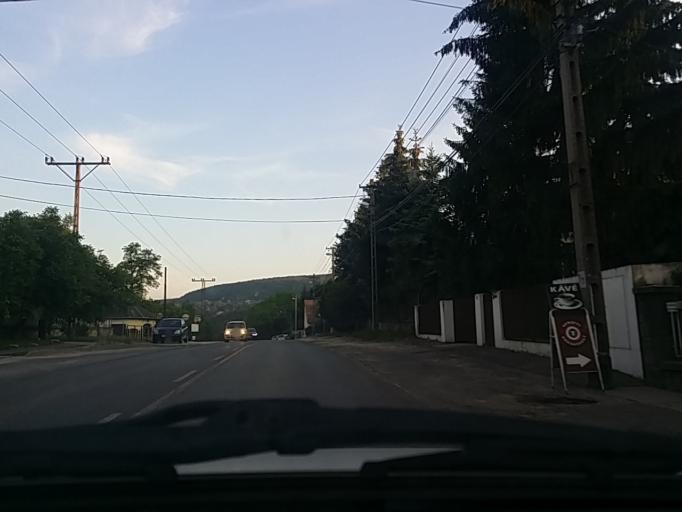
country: HU
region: Pest
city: Solymar
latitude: 47.5822
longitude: 18.9391
